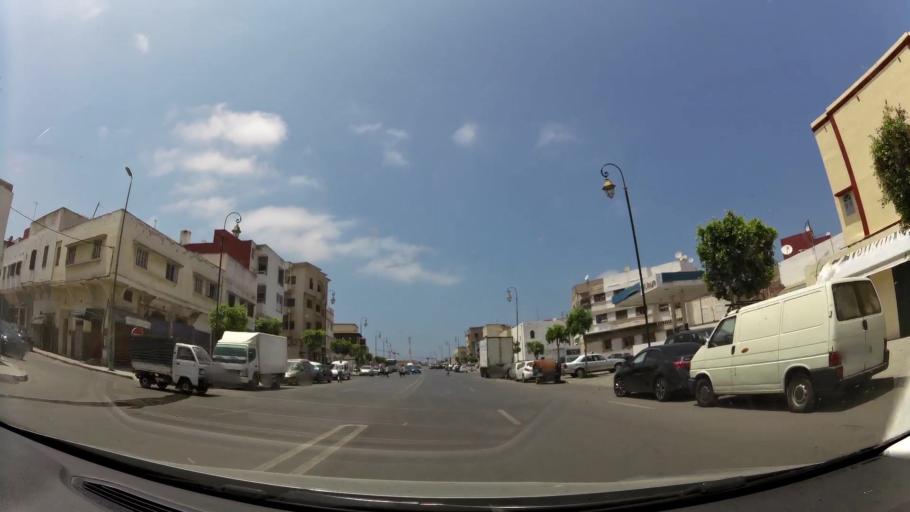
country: MA
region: Rabat-Sale-Zemmour-Zaer
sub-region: Rabat
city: Rabat
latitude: 34.0097
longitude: -6.8566
